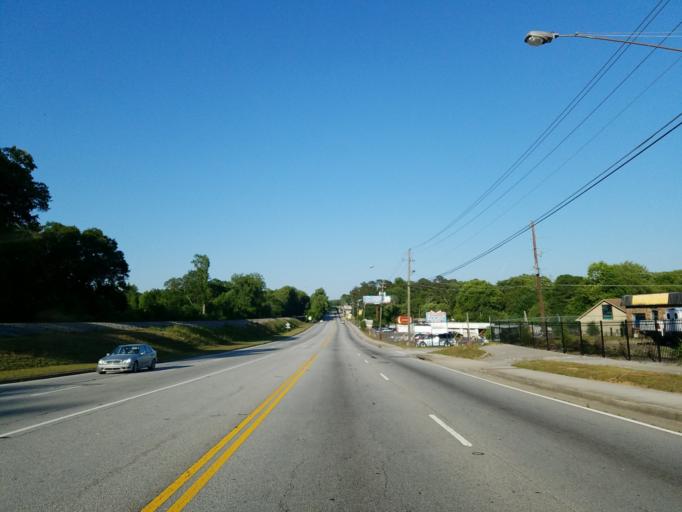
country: US
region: Georgia
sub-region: Cobb County
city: Austell
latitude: 33.8144
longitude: -84.6261
